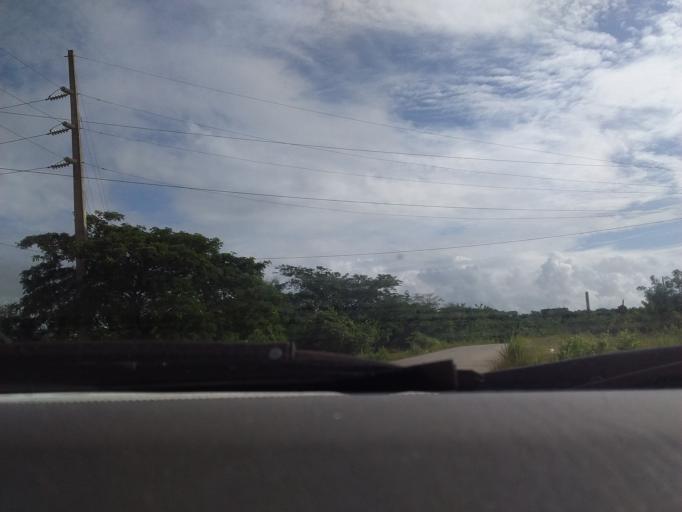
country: DO
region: Santo Domingo
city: Guerra
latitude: 18.5595
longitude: -69.7886
